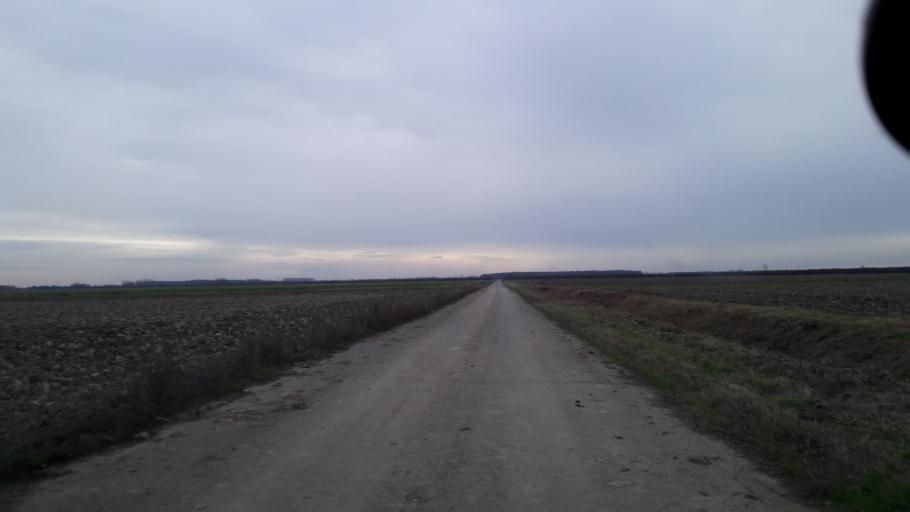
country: HR
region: Osjecko-Baranjska
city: Vladislavci
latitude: 45.4400
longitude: 18.5672
